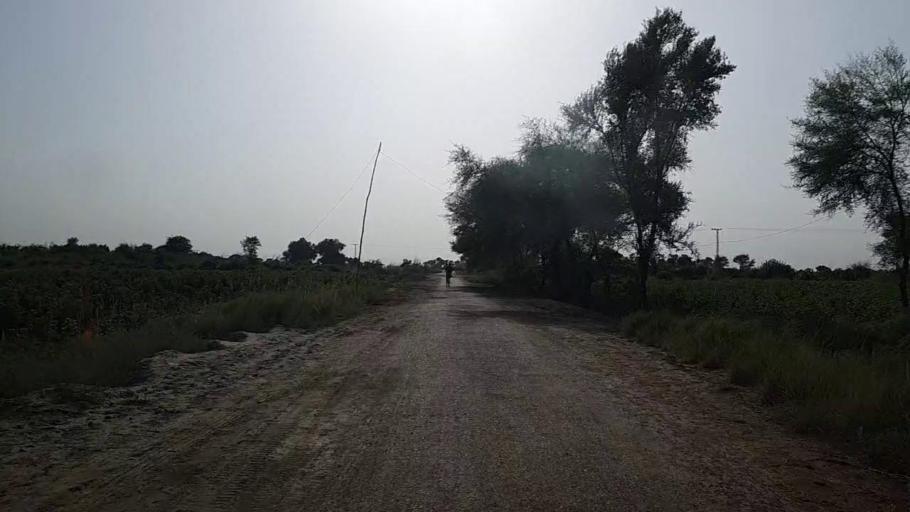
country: PK
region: Sindh
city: Pad Idan
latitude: 26.8532
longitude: 68.3174
